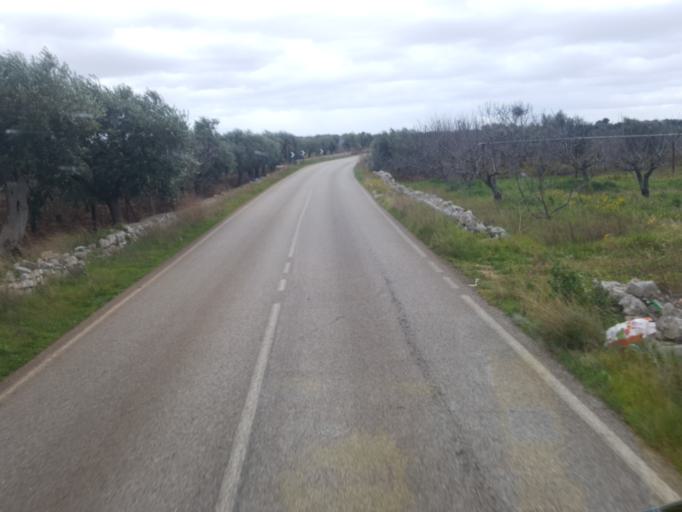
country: IT
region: Apulia
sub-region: Provincia di Bari
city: Conversano
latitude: 40.9440
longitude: 17.0768
